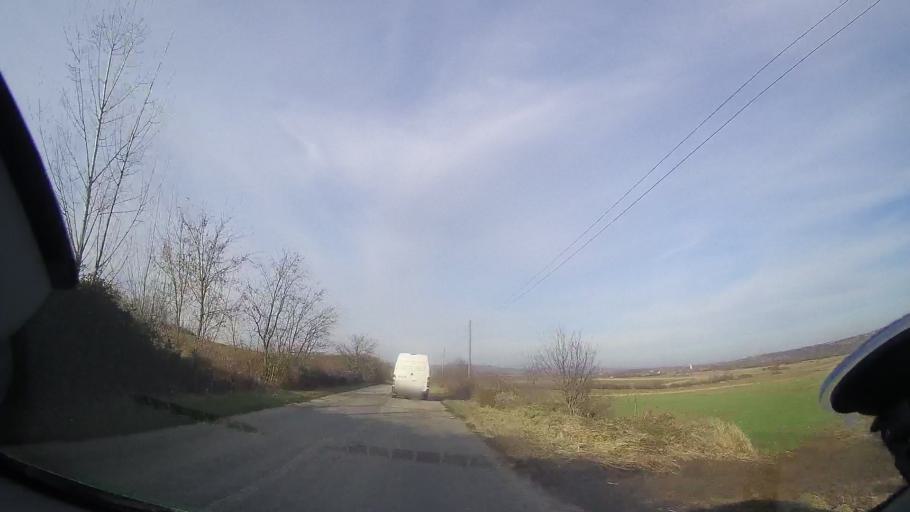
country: RO
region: Bihor
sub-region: Comuna Spinus
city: Spinus
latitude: 47.2046
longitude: 22.1826
